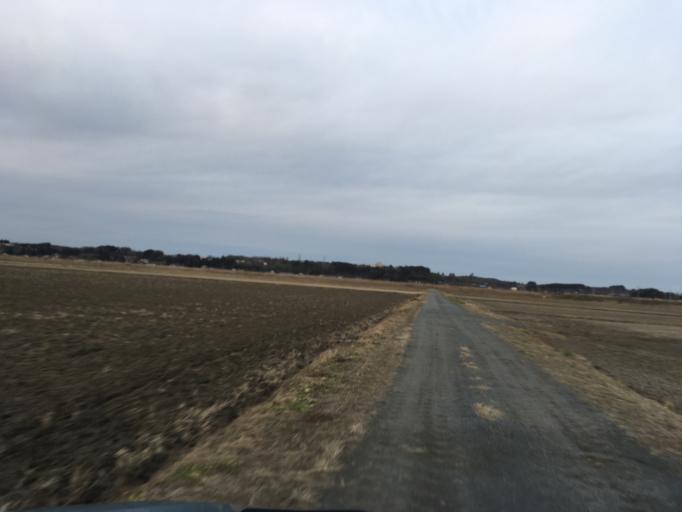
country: JP
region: Miyagi
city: Kogota
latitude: 38.6402
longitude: 141.0671
